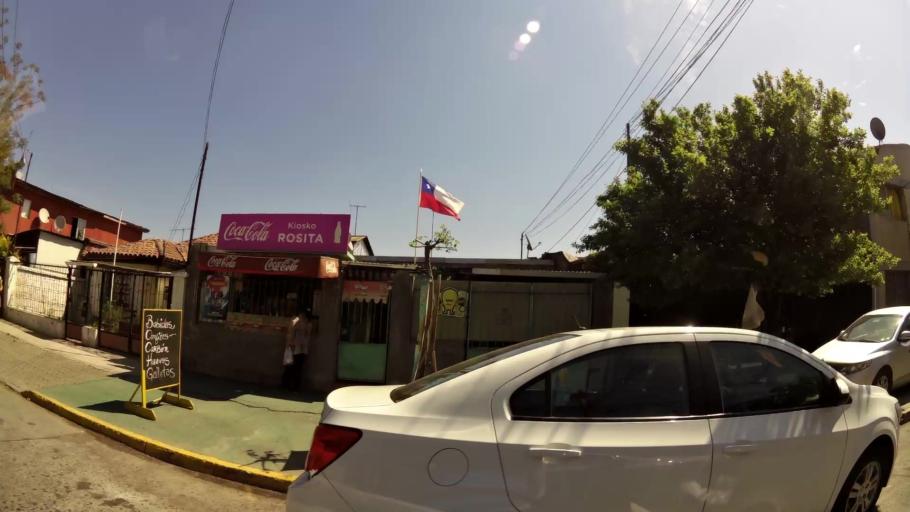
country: CL
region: Santiago Metropolitan
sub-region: Provincia de Santiago
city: La Pintana
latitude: -33.5317
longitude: -70.6470
